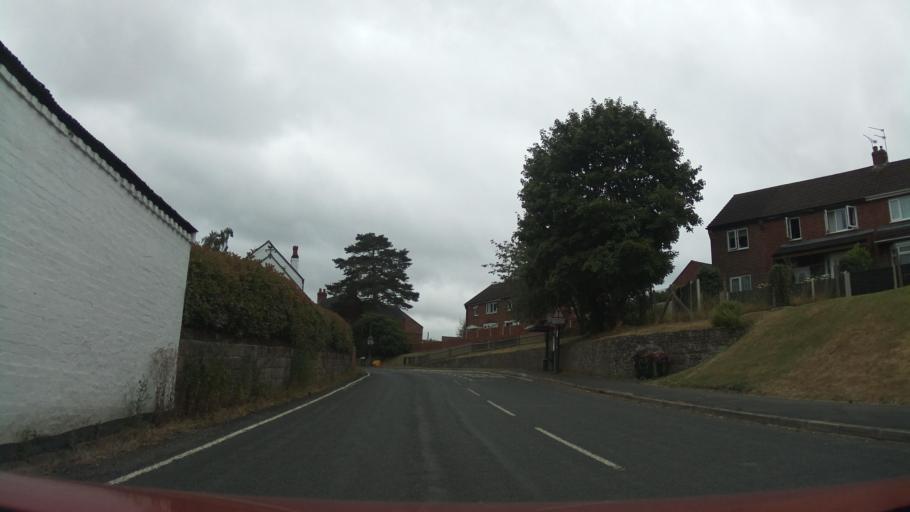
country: GB
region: England
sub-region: Derbyshire
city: Findern
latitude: 52.8717
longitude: -1.5440
